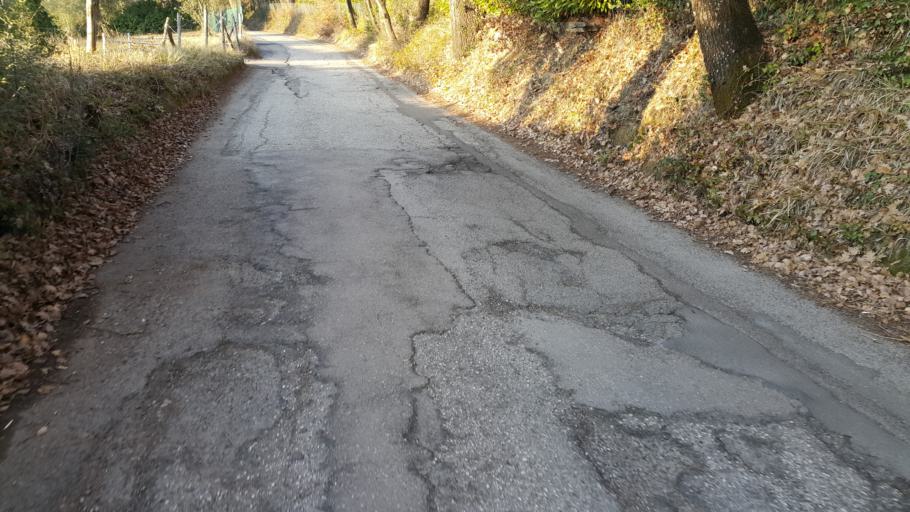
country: IT
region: Umbria
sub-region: Provincia di Perugia
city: Perugia
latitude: 43.0876
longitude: 12.3780
